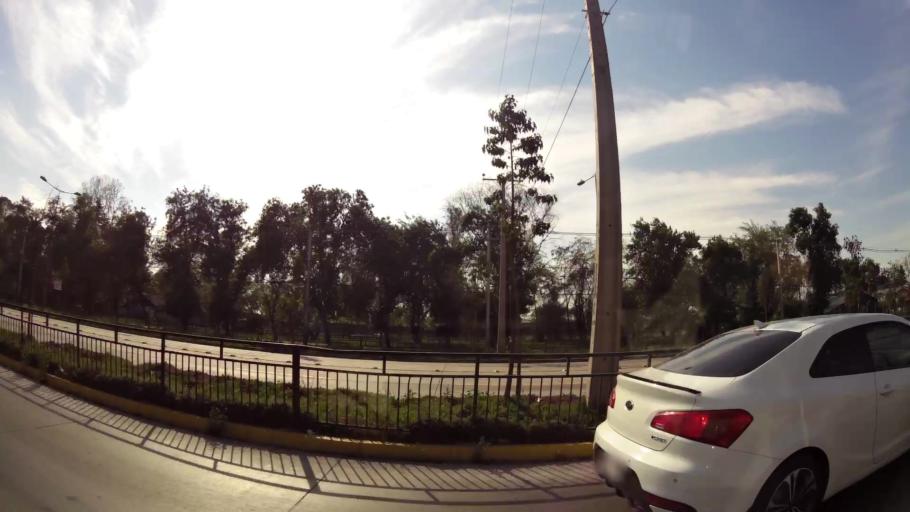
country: CL
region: Santiago Metropolitan
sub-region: Provincia de Santiago
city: La Pintana
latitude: -33.5627
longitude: -70.6306
